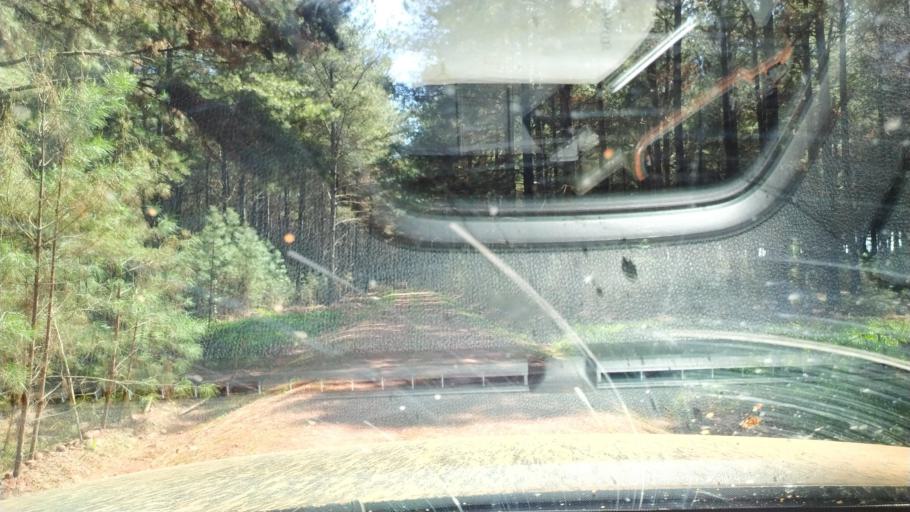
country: AR
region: Corrientes
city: Santo Tome
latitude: -28.4637
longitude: -55.9944
